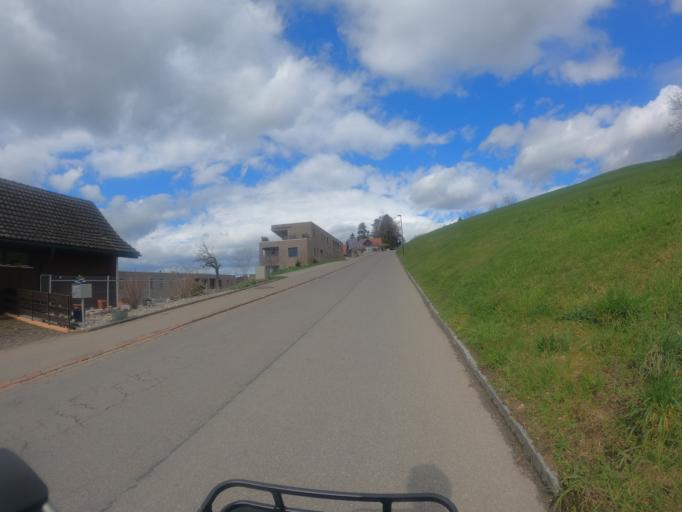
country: CH
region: Zurich
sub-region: Bezirk Affoltern
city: Mettmenstetten
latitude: 47.2483
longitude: 8.4691
